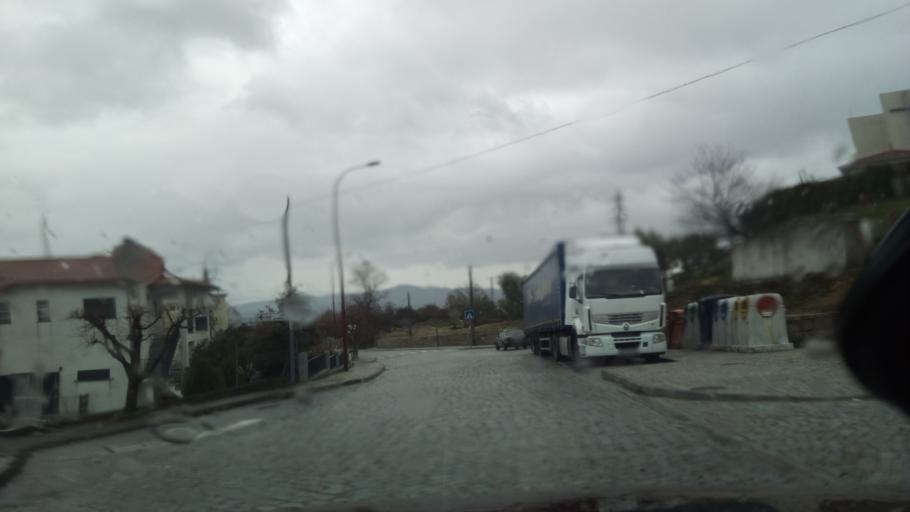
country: PT
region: Guarda
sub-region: Celorico da Beira
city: Celorico da Beira
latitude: 40.6422
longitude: -7.3898
